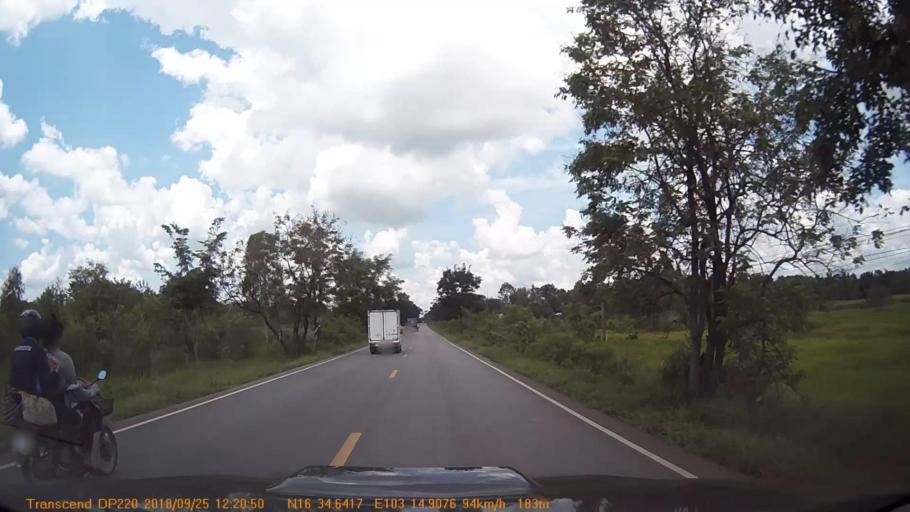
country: TH
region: Kalasin
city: Huai Mek
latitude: 16.5774
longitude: 103.2484
